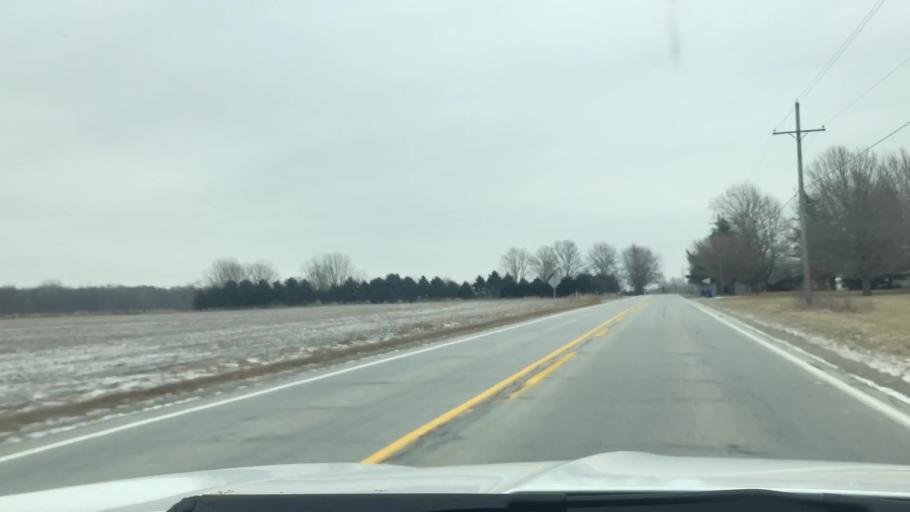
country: US
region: Indiana
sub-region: Fulton County
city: Rochester
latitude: 41.0572
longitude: -86.1662
